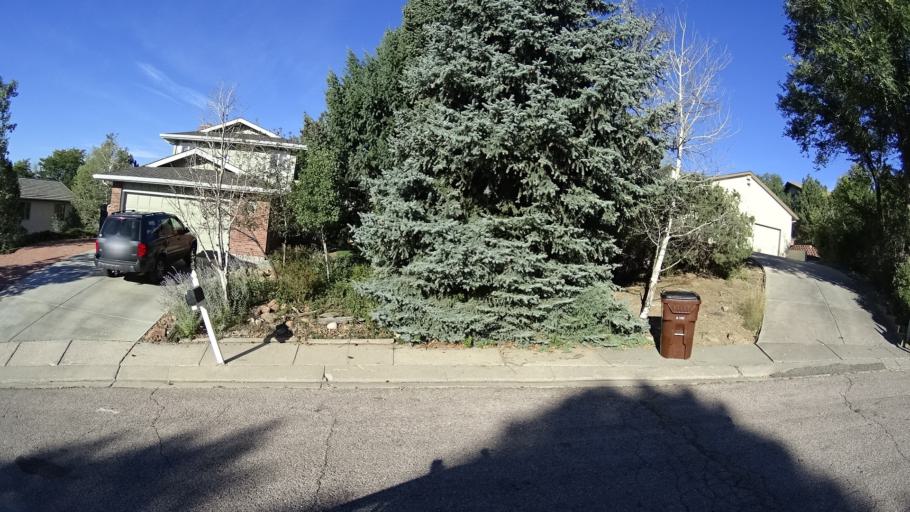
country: US
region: Colorado
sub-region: El Paso County
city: Cimarron Hills
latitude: 38.9125
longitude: -104.7551
